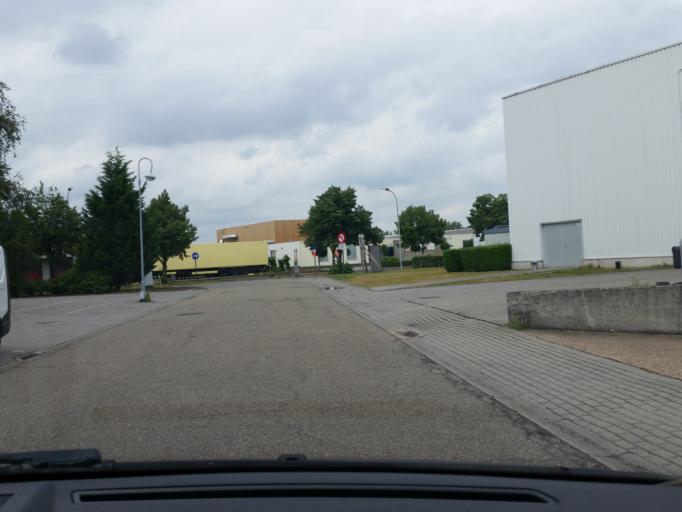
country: BE
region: Flanders
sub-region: Provincie Antwerpen
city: Rumst
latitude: 51.0497
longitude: 4.4450
